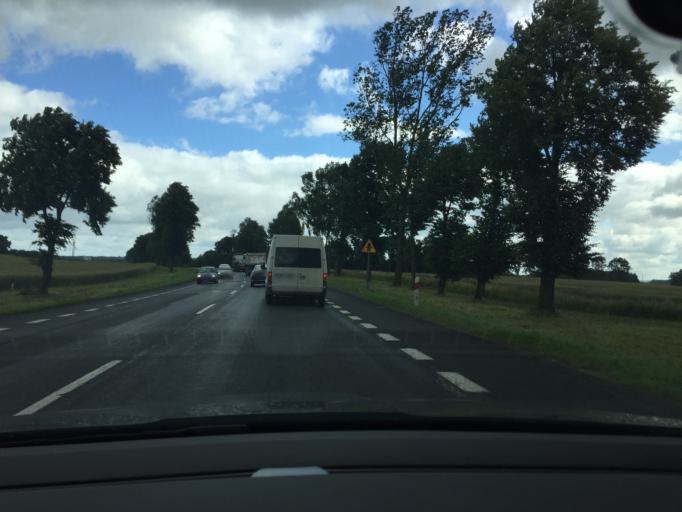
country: PL
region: West Pomeranian Voivodeship
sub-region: Koszalin
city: Koszalin
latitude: 54.1513
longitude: 16.0758
